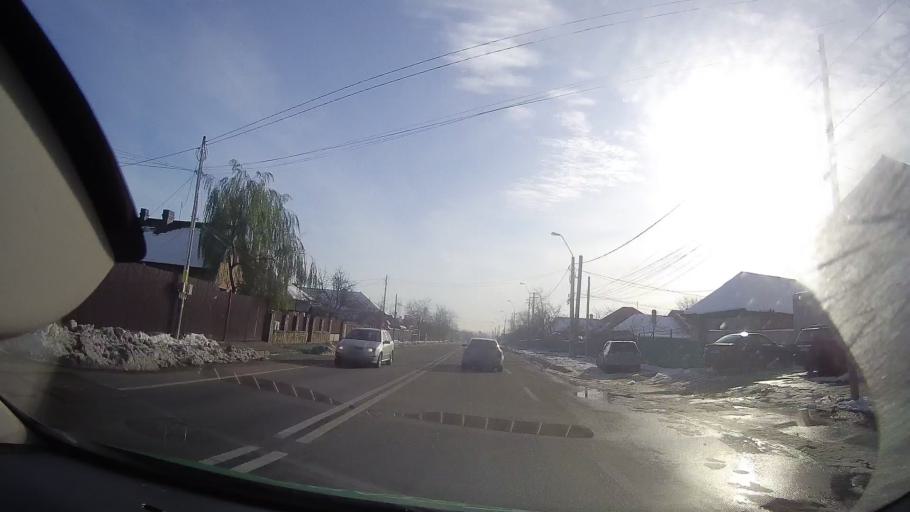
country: RO
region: Neamt
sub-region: Comuna Garcina
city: Garcina
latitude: 46.9586
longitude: 26.3826
